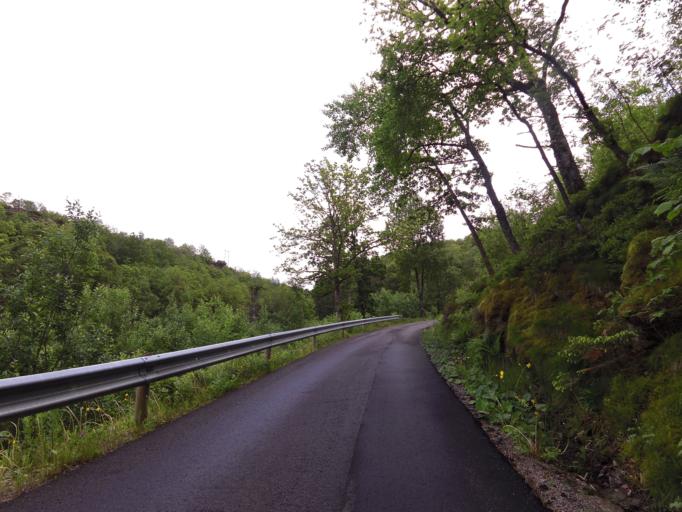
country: NO
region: Vest-Agder
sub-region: Lyngdal
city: Lyngdal
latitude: 58.0994
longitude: 6.9613
